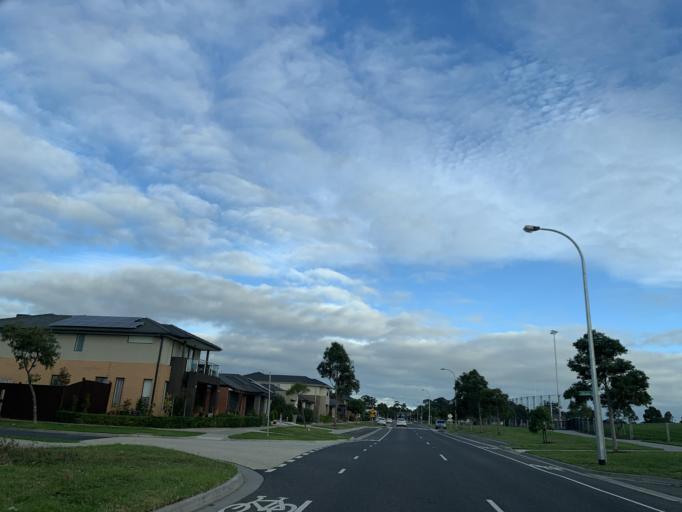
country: AU
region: Victoria
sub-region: Casey
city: Cranbourne East
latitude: -38.1239
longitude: 145.2974
